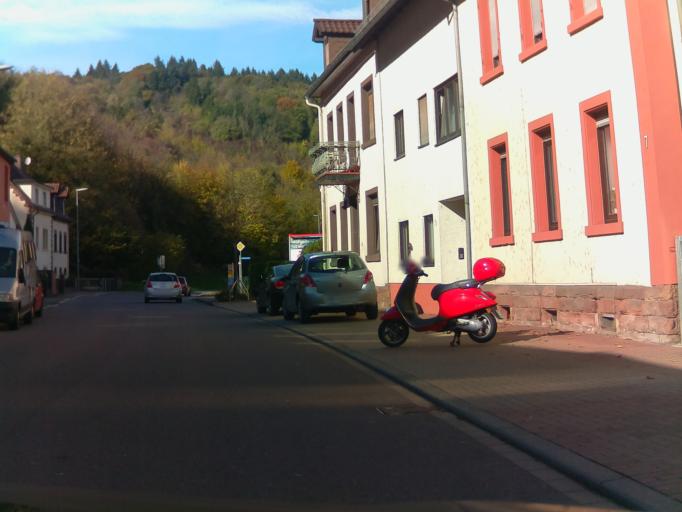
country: DE
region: Baden-Wuerttemberg
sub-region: Karlsruhe Region
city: Joehlingen
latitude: 48.9882
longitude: 8.5364
